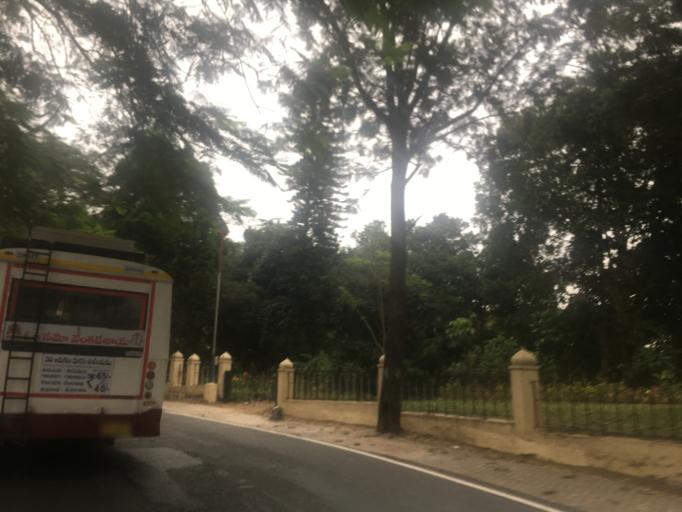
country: IN
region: Andhra Pradesh
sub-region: Chittoor
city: Tirumala
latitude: 13.6686
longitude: 79.3502
